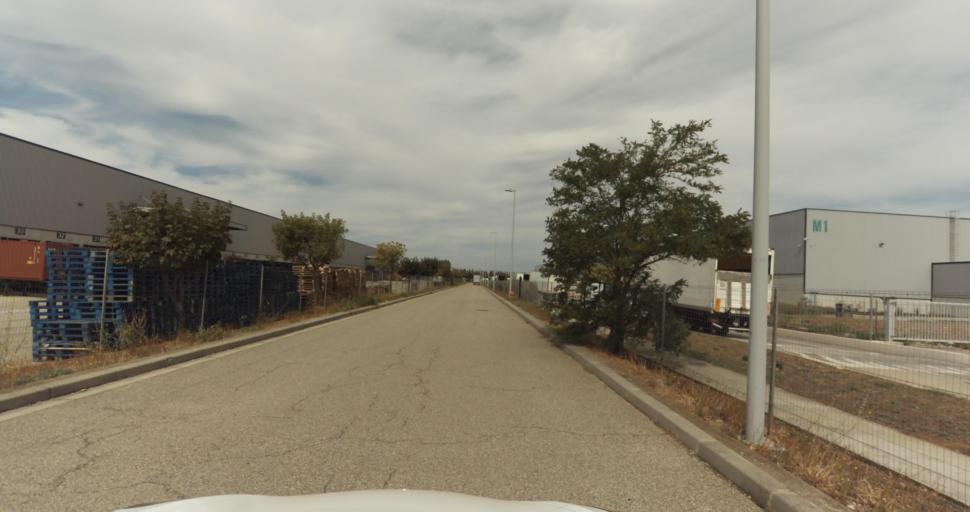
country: FR
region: Provence-Alpes-Cote d'Azur
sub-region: Departement des Bouches-du-Rhone
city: Miramas
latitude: 43.6086
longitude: 4.9976
